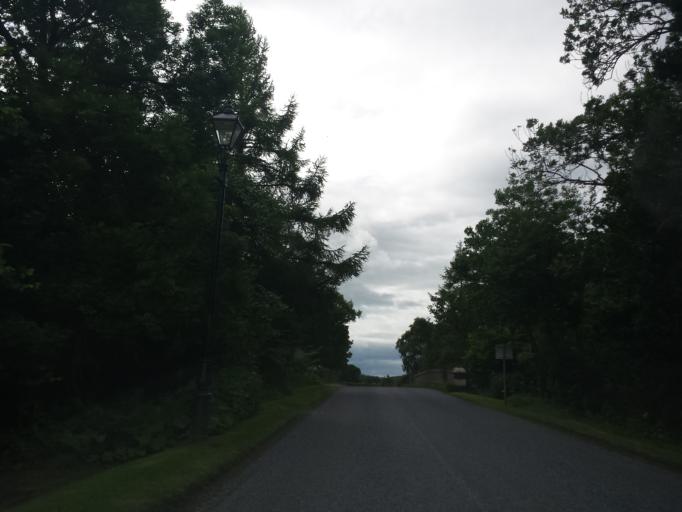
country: GB
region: Scotland
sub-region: Highland
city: Nairn
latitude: 57.5276
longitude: -3.9271
